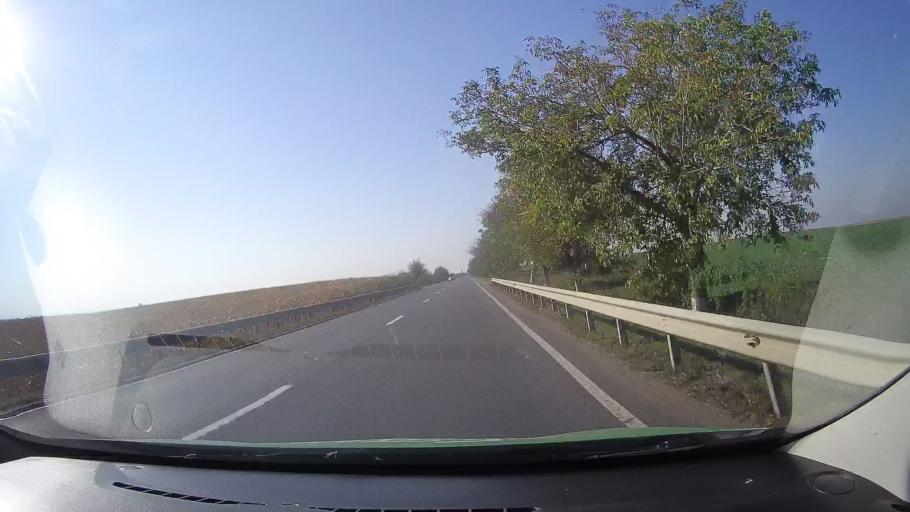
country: RO
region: Satu Mare
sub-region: Comuna Petresti
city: Petresti
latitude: 47.6228
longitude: 22.3839
